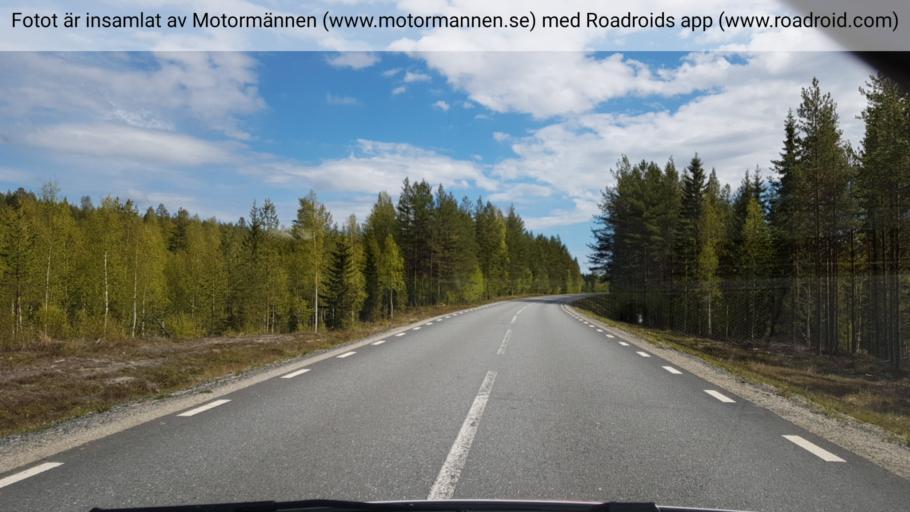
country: SE
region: Vaesterbotten
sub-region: Bjurholms Kommun
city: Bjurholm
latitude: 64.2911
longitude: 19.1897
